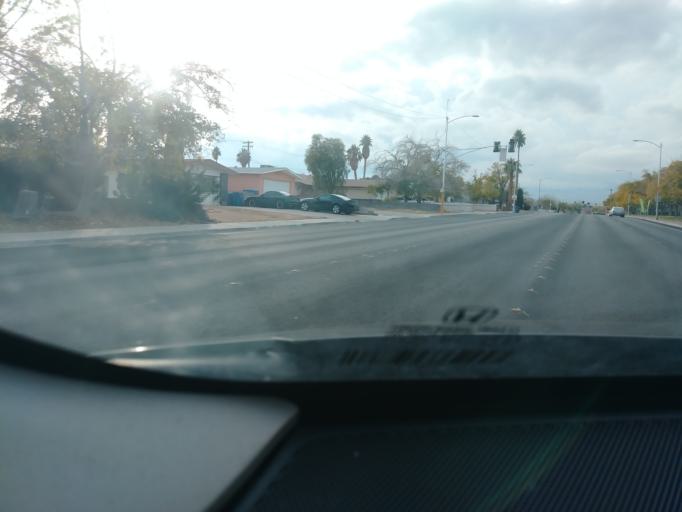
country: US
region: Nevada
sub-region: Clark County
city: Spring Valley
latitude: 36.1809
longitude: -115.2200
